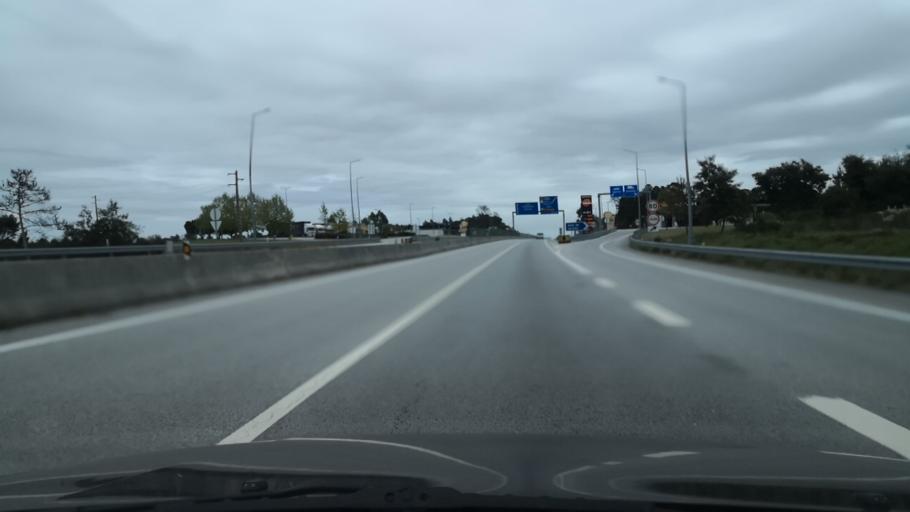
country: PT
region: Viseu
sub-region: Viseu
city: Viseu
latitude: 40.6242
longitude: -7.9353
